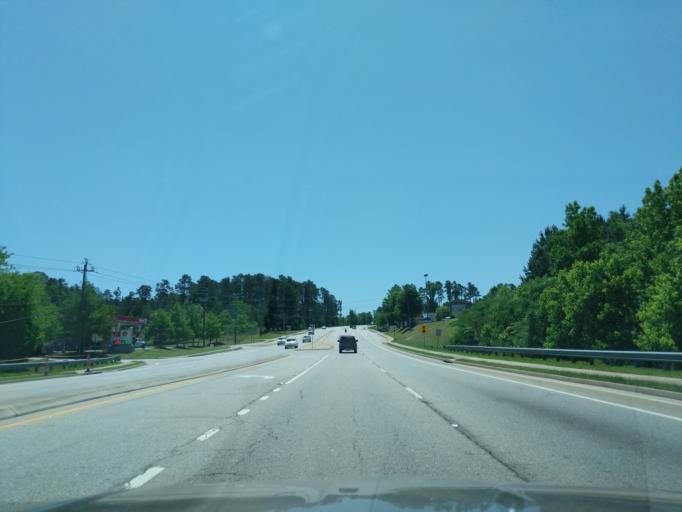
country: US
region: Georgia
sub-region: Columbia County
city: Martinez
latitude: 33.5386
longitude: -82.0804
